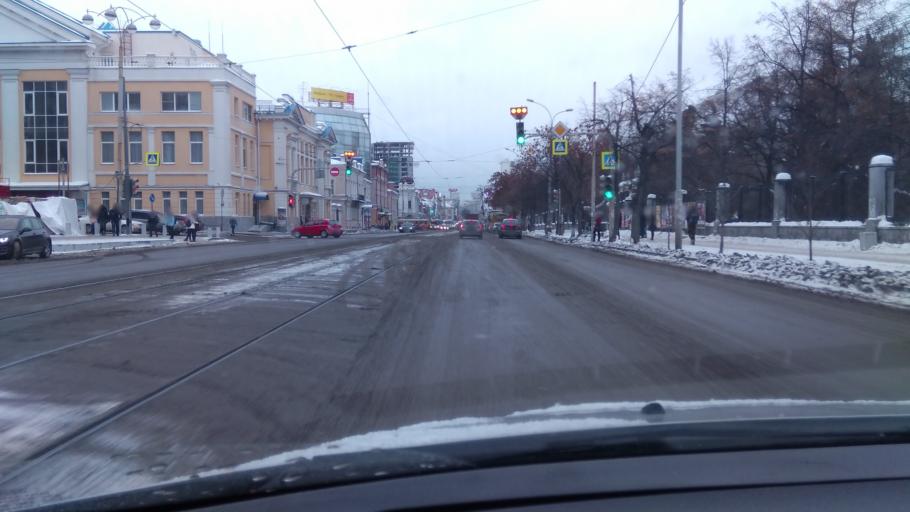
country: RU
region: Sverdlovsk
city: Yekaterinburg
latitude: 56.8287
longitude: 60.6018
